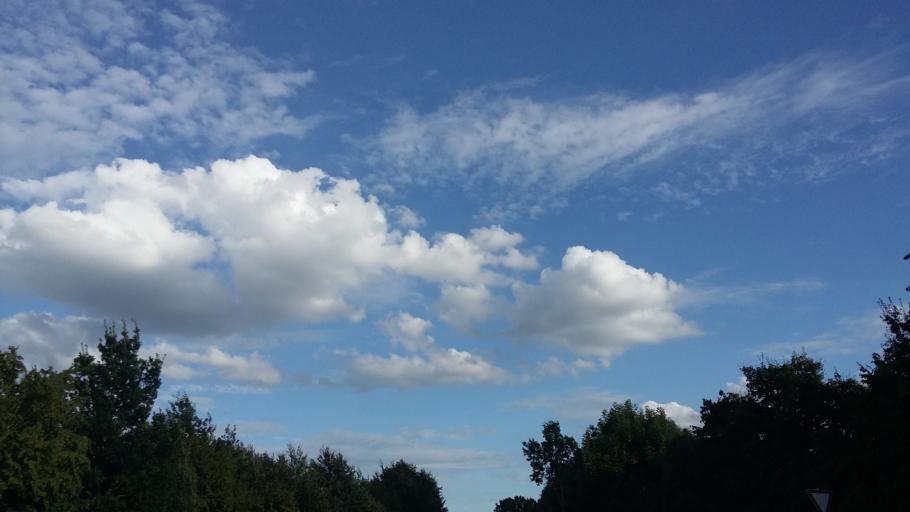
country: DE
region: Bavaria
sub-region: Swabia
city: Merching
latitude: 48.2529
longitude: 10.9871
